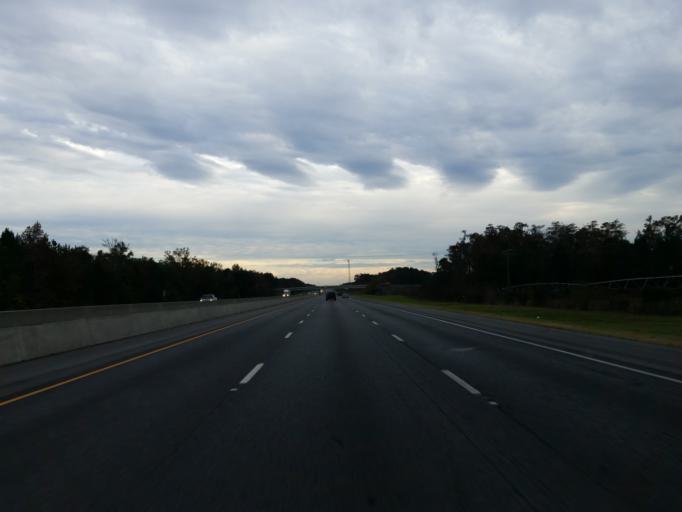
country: US
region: Georgia
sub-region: Lowndes County
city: Hahira
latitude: 30.9557
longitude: -83.3770
